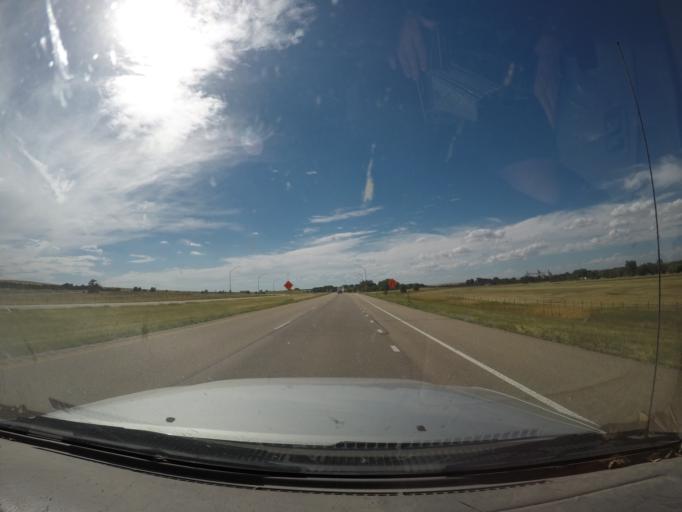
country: US
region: Nebraska
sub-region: Deuel County
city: Chappell
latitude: 41.0781
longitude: -102.4682
